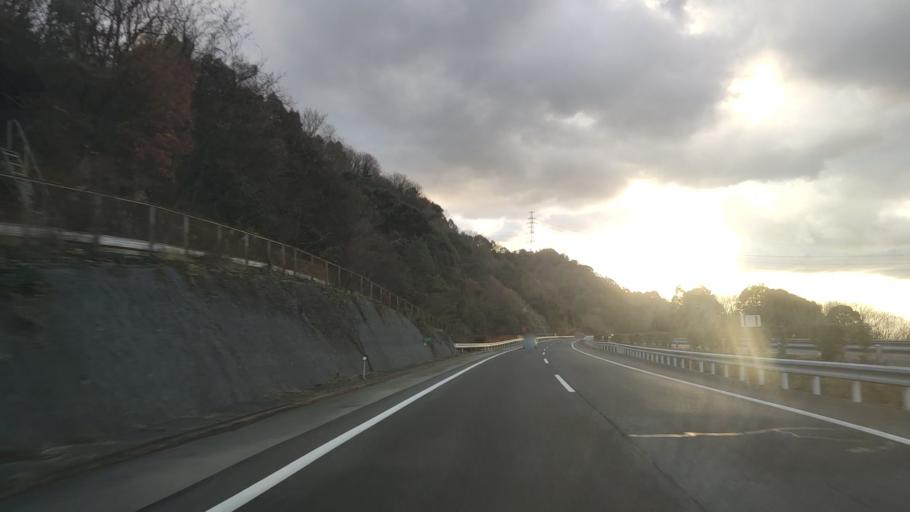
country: JP
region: Ehime
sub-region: Shikoku-chuo Shi
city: Matsuyama
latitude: 33.8139
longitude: 132.9557
